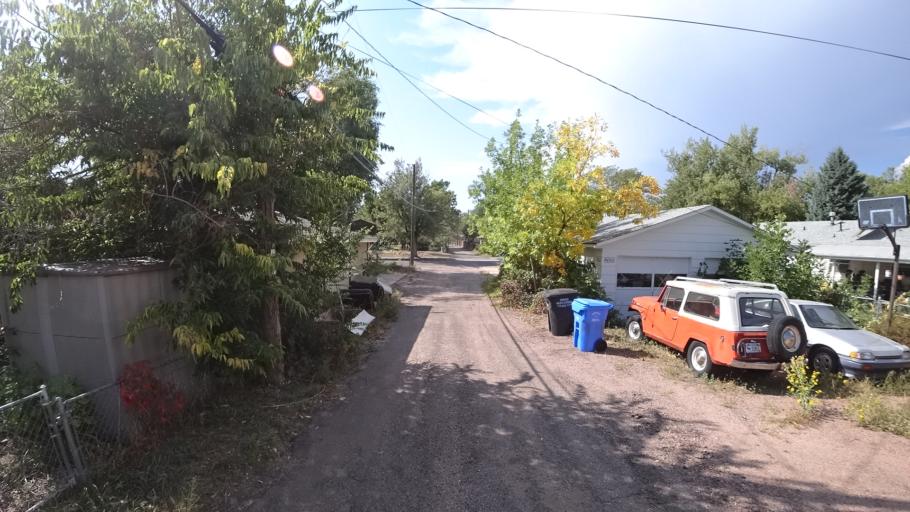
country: US
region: Colorado
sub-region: El Paso County
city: Colorado Springs
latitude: 38.8630
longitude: -104.7737
